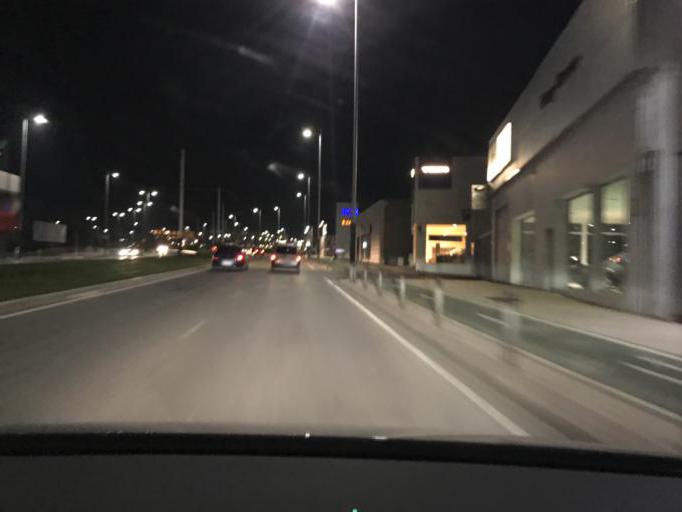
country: ES
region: Andalusia
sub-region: Provincia de Jaen
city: Jaen
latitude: 37.7937
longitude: -3.7804
